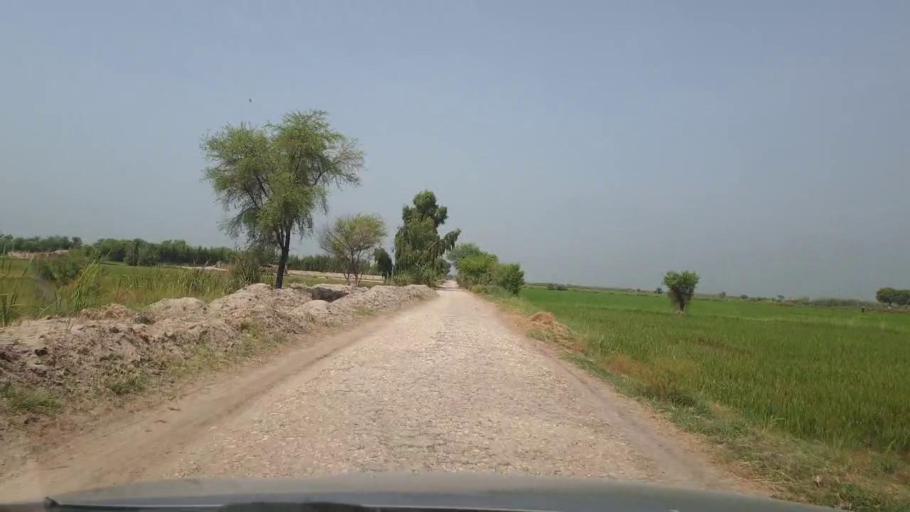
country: PK
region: Sindh
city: Garhi Yasin
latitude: 27.9103
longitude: 68.4005
